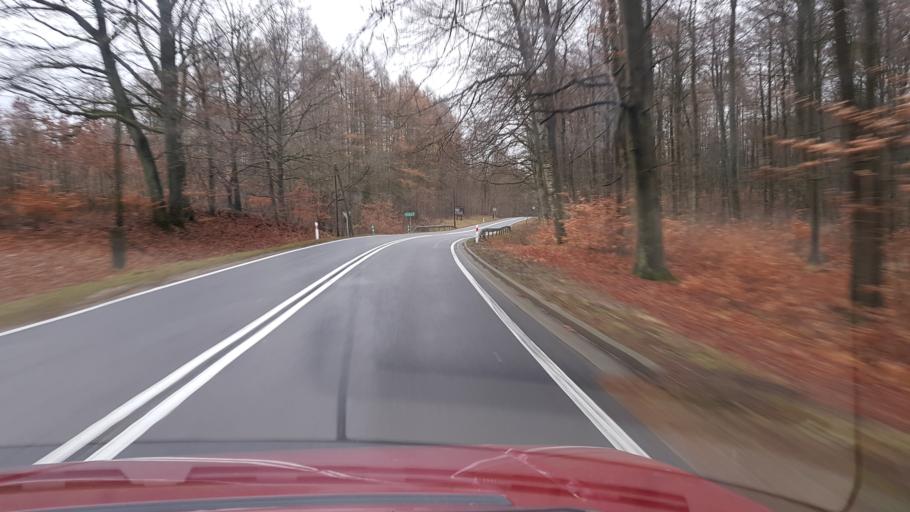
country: PL
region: West Pomeranian Voivodeship
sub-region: Powiat lobeski
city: Wegorzyno
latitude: 53.5250
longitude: 15.6085
